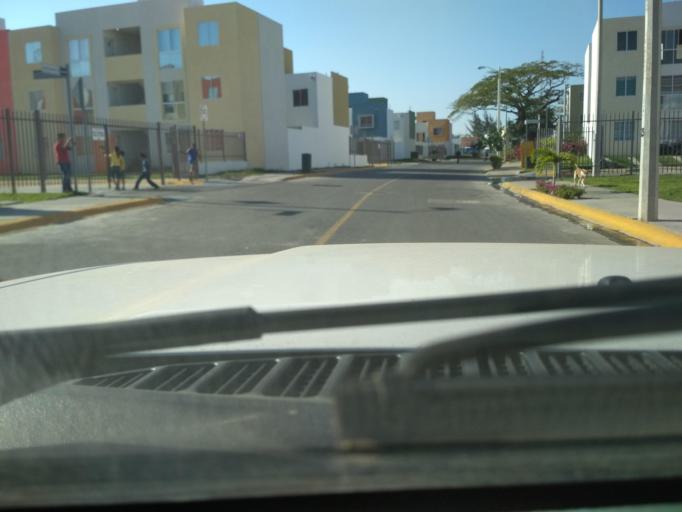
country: MX
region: Veracruz
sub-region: Veracruz
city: Las Amapolas
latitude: 19.1462
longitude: -96.2348
